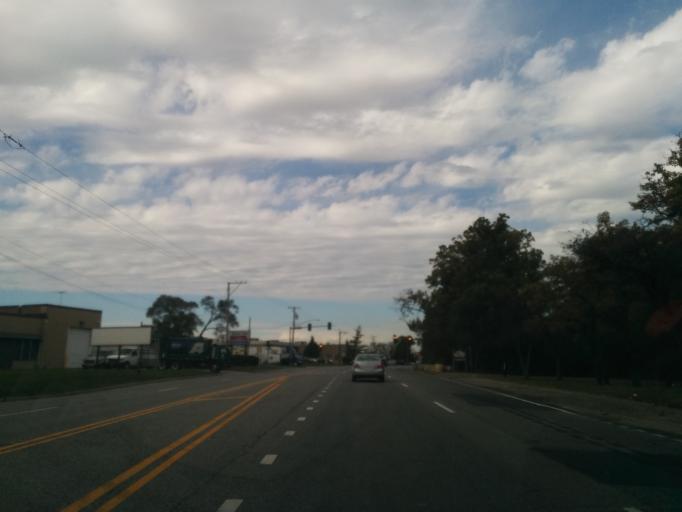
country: US
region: Illinois
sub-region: Cook County
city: Franklin Park
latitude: 41.9459
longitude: -87.8553
